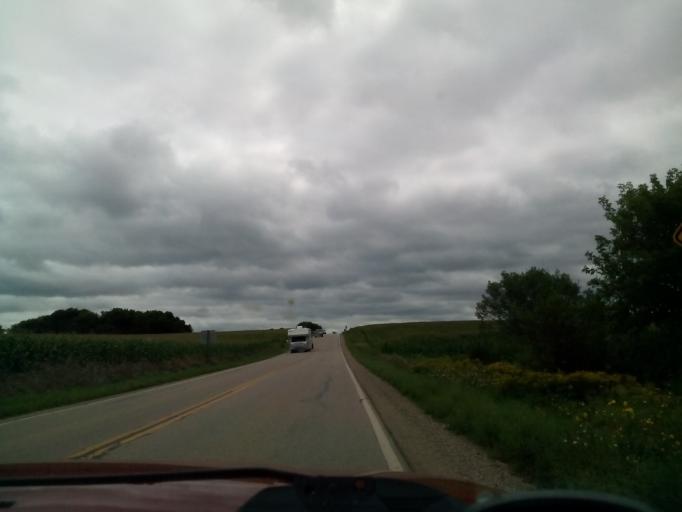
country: US
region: Wisconsin
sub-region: Oconto County
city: Gillett
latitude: 45.0033
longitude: -88.4175
